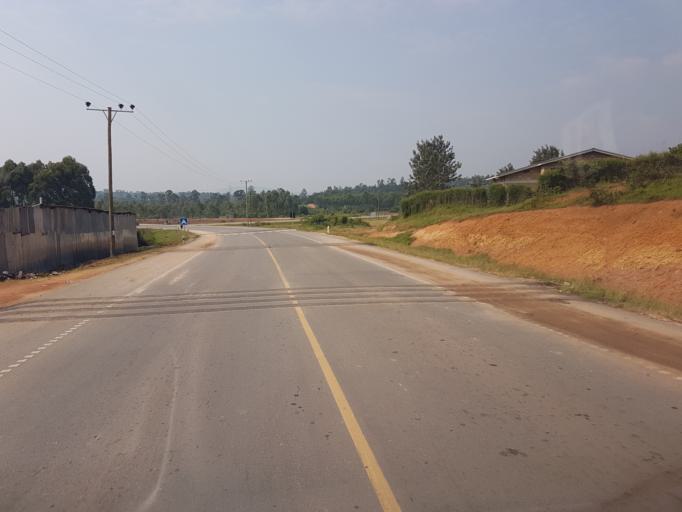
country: UG
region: Western Region
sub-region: Mbarara District
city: Bwizibwera
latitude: -0.6359
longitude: 30.6030
